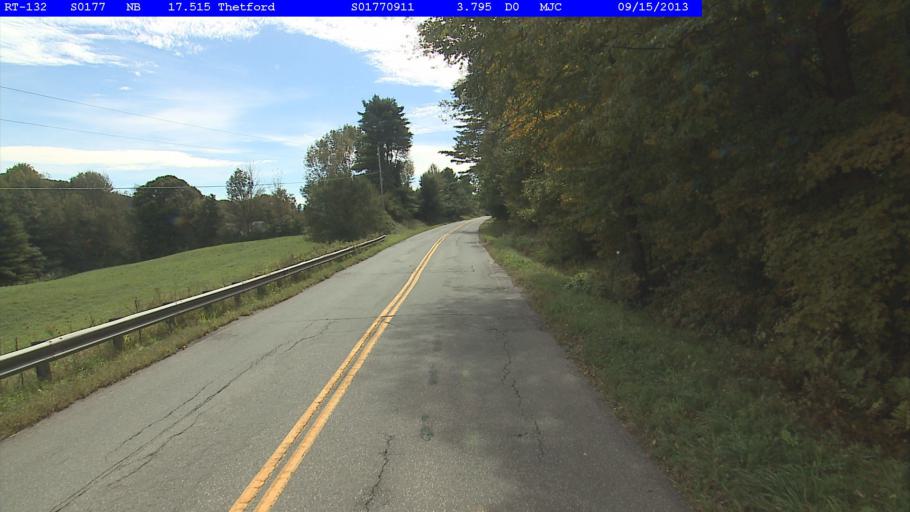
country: US
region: New Hampshire
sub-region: Grafton County
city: Hanover
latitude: 43.8048
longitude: -72.2684
